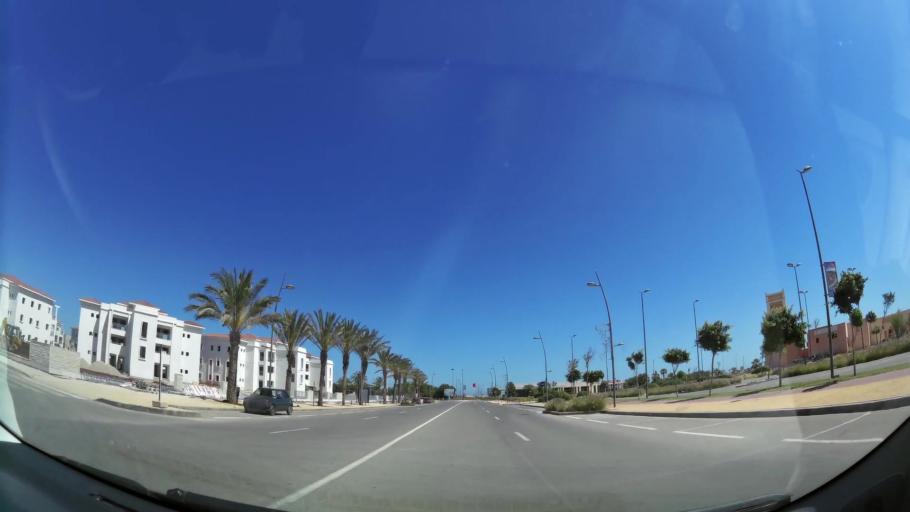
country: MA
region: Oriental
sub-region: Berkane-Taourirt
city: Madagh
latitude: 35.1079
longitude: -2.2996
